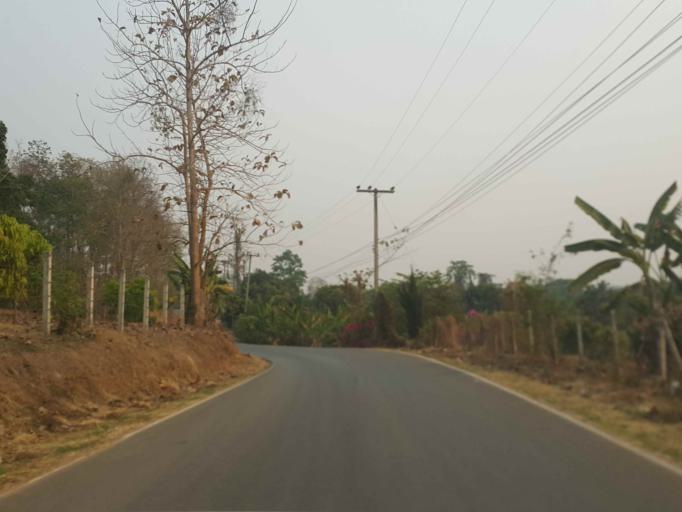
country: TH
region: Chiang Mai
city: Mae Taeng
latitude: 19.1118
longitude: 98.8961
